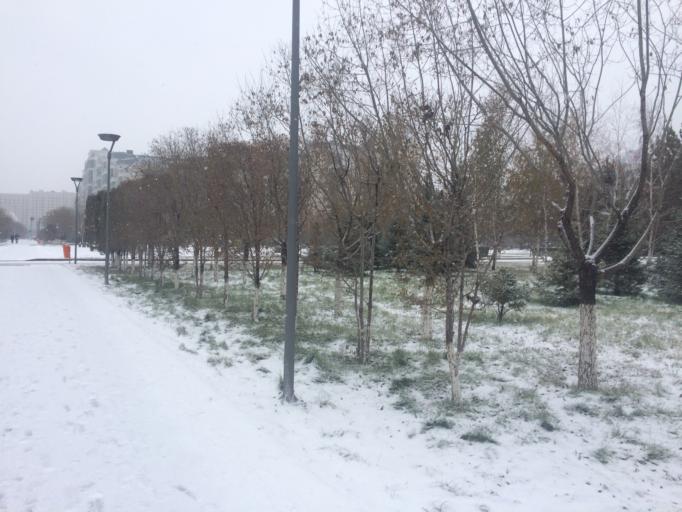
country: KZ
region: Astana Qalasy
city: Astana
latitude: 51.1306
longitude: 71.4311
